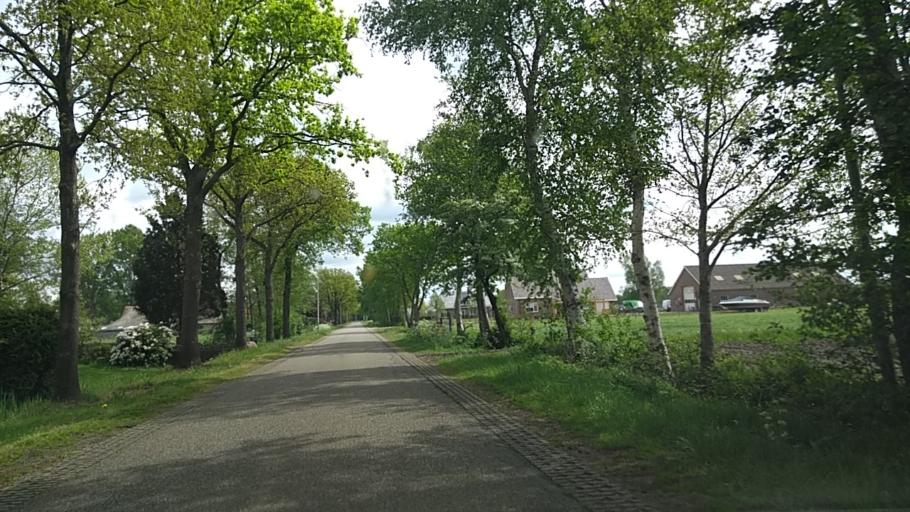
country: NL
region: Overijssel
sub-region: Gemeente Staphorst
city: Staphorst
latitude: 52.6090
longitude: 6.2478
